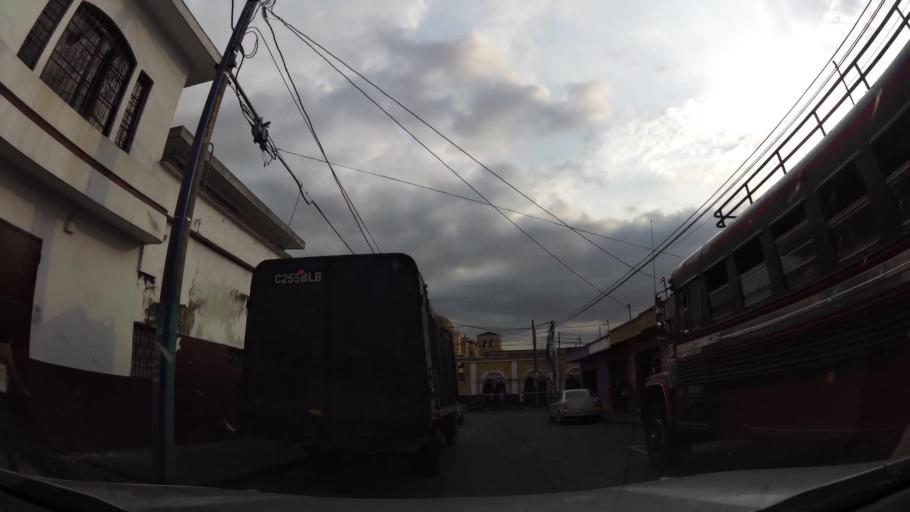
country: GT
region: Escuintla
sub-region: Municipio de Escuintla
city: Escuintla
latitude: 14.3026
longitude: -90.7854
